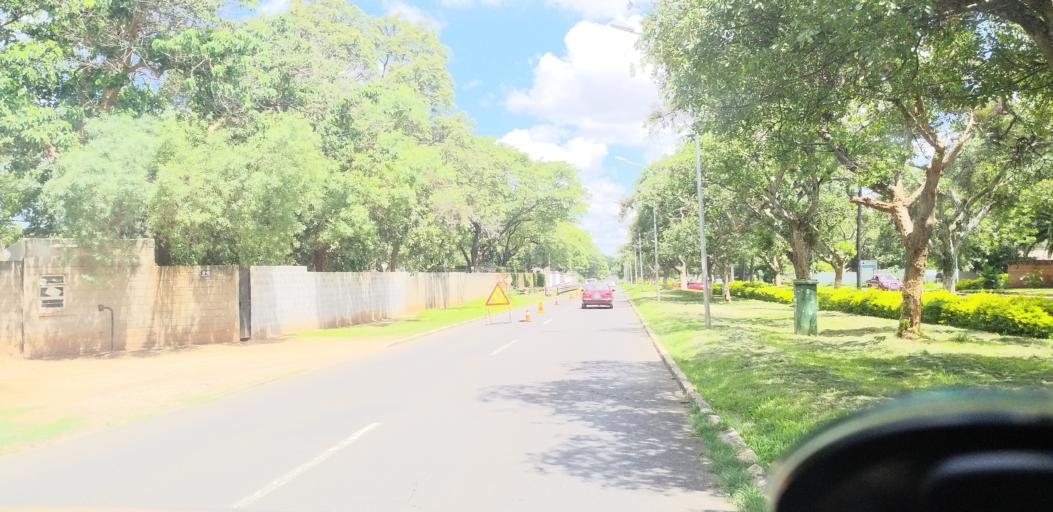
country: ZM
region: Lusaka
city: Lusaka
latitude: -15.4289
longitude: 28.3218
